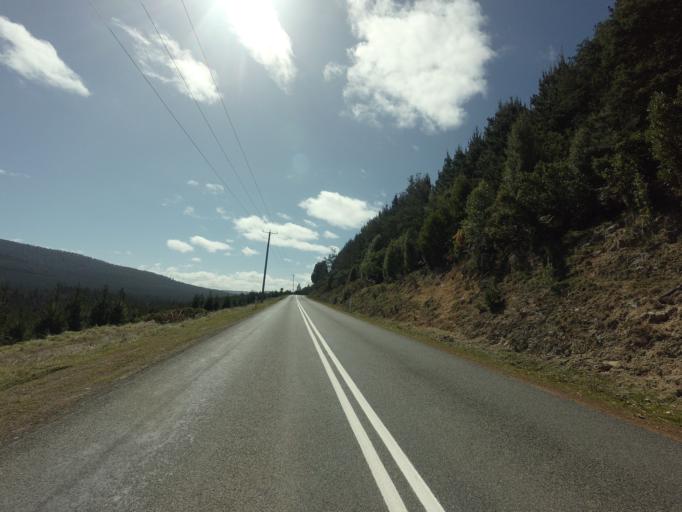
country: AU
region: Tasmania
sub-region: Derwent Valley
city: New Norfolk
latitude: -42.7450
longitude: 146.6540
